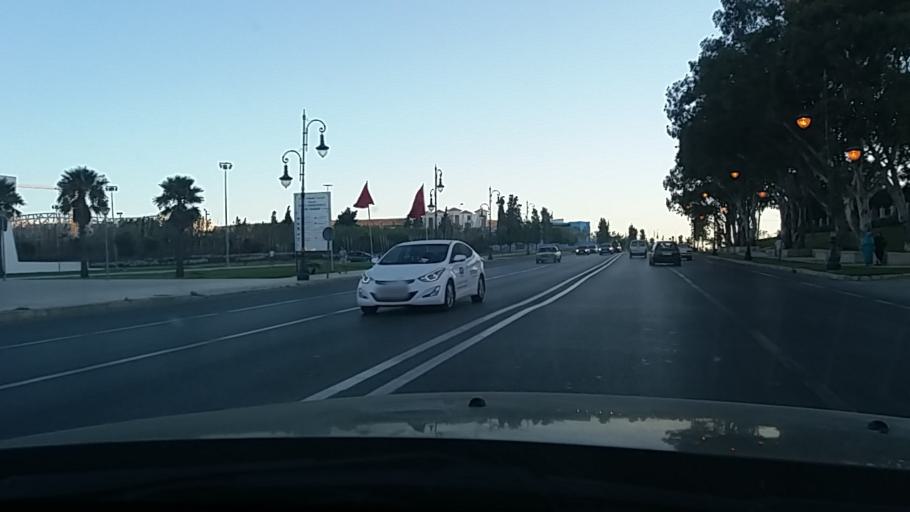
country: MA
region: Tanger-Tetouan
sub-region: Tanger-Assilah
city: Boukhalef
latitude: 35.7461
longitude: -5.8615
